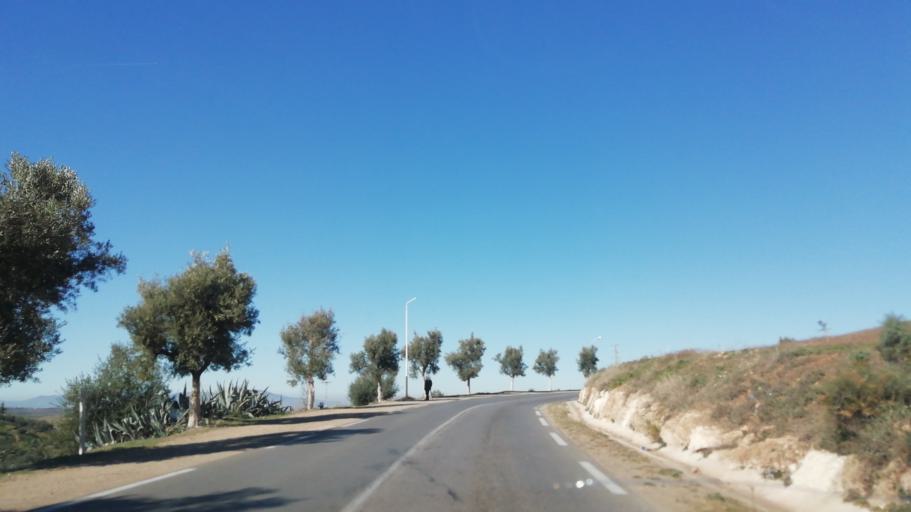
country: DZ
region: Tlemcen
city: Beni Mester
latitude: 34.8414
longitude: -1.4762
